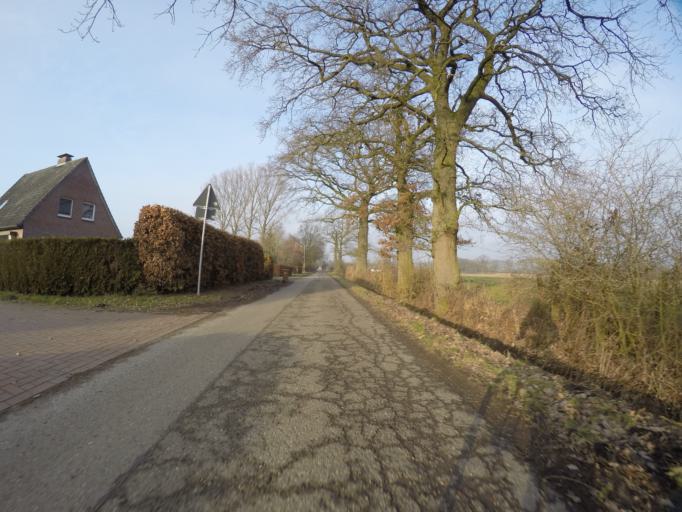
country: DE
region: Schleswig-Holstein
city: Quickborn
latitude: 53.7111
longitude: 9.8934
